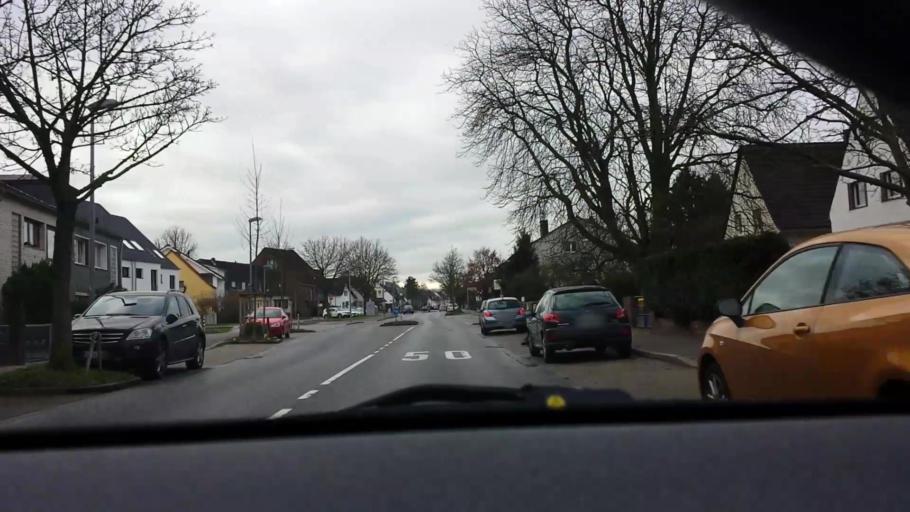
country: DE
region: North Rhine-Westphalia
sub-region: Regierungsbezirk Dusseldorf
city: Dusseldorf
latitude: 51.1819
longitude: 6.8170
